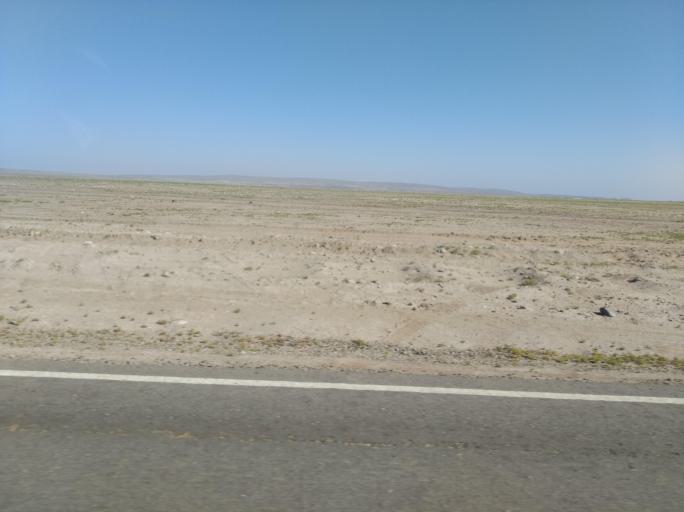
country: CL
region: Atacama
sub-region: Provincia de Copiapo
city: Copiapo
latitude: -27.3166
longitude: -70.8664
